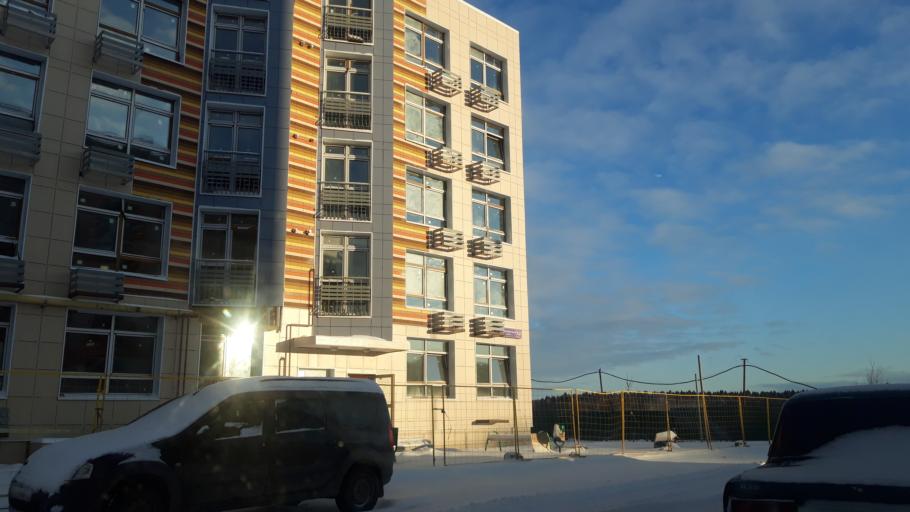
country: RU
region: Moskovskaya
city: Novopodrezkovo
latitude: 55.9084
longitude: 37.3278
